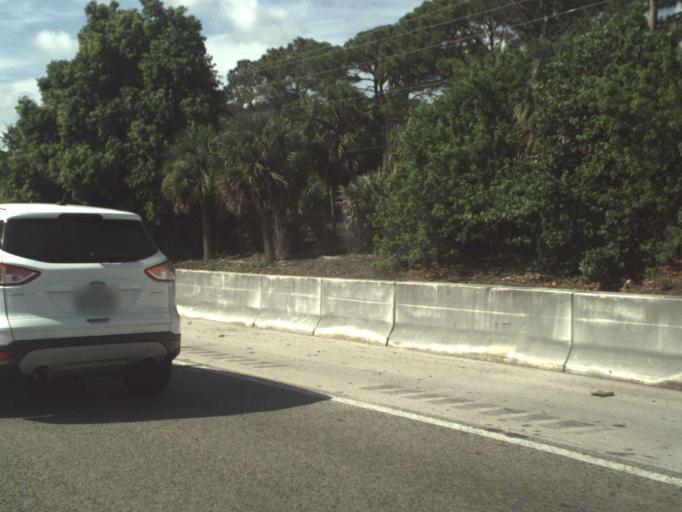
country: US
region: Florida
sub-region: Palm Beach County
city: North Palm Beach
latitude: 26.8346
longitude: -80.0989
